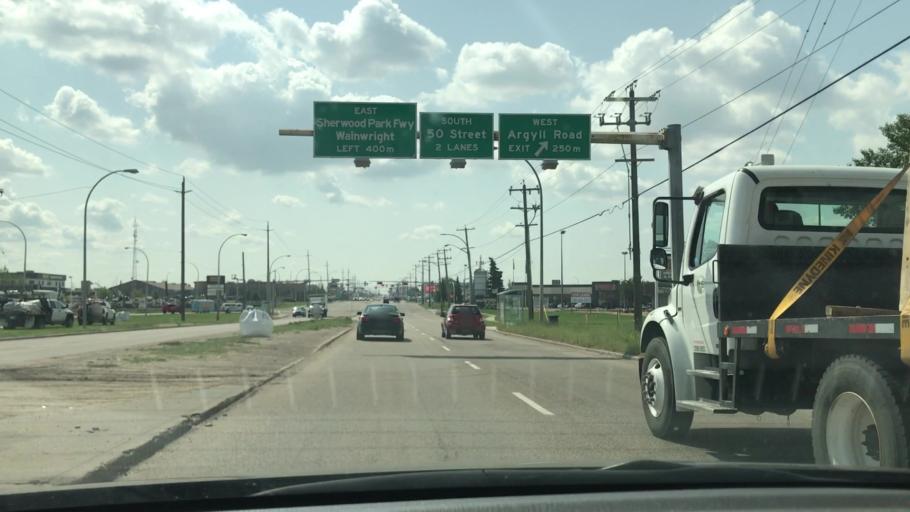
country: CA
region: Alberta
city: Edmonton
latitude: 53.5177
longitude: -113.4186
